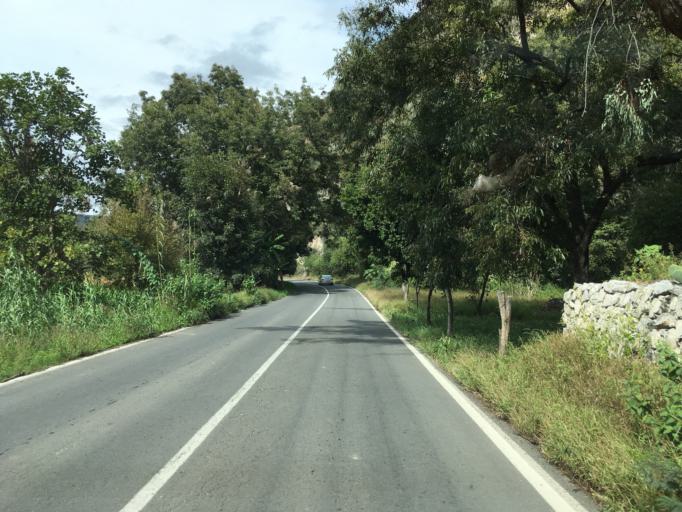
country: MX
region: Hidalgo
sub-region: San Agustin Metzquititlan
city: Mezquititlan
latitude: 20.5355
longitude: -98.7204
